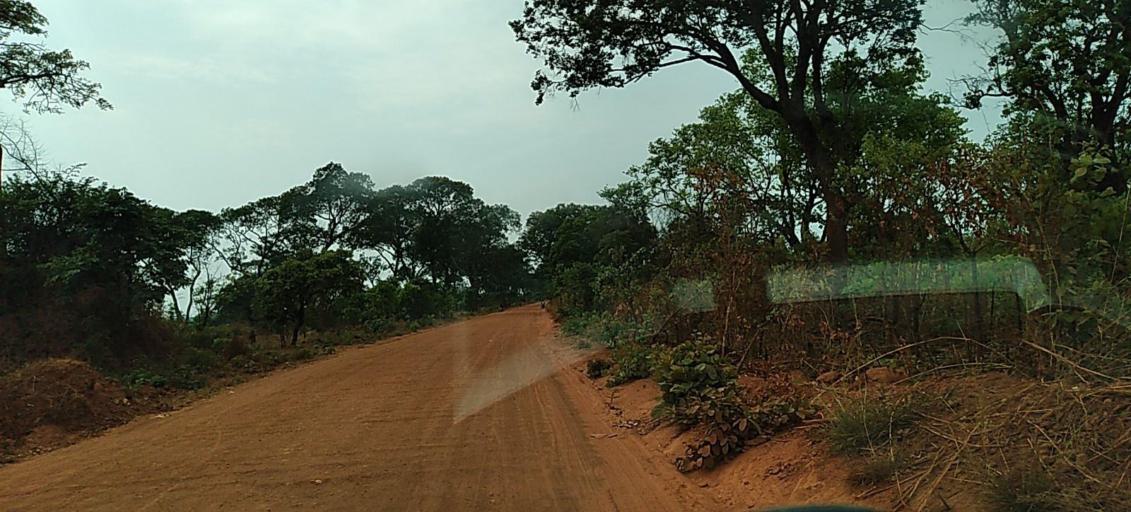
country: ZM
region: North-Western
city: Solwezi
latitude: -12.2072
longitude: 26.4986
